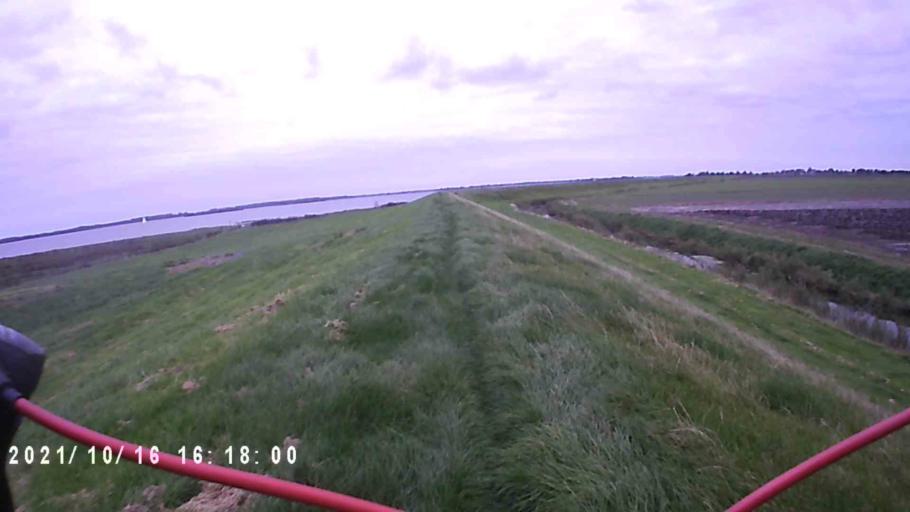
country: NL
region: Friesland
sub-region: Gemeente Dongeradeel
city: Anjum
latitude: 53.3921
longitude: 6.1510
